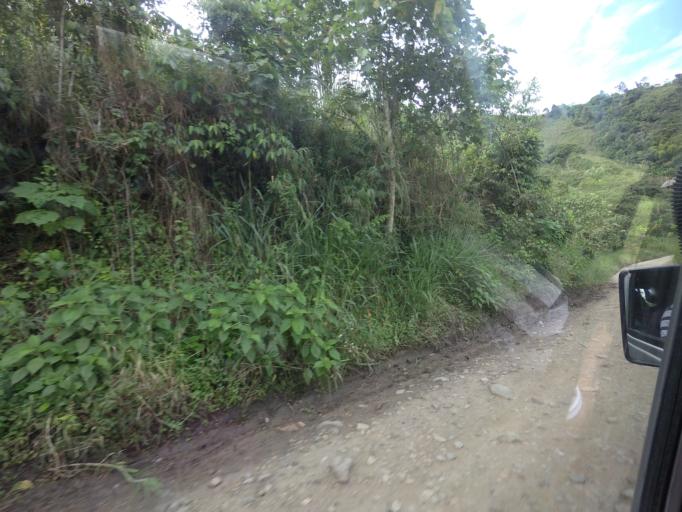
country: CO
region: Huila
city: San Agustin
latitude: 1.9219
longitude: -76.2971
